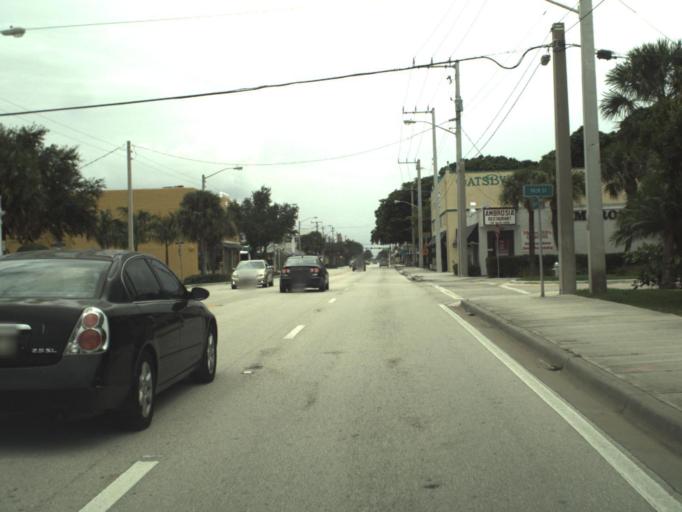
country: US
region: Florida
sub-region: Palm Beach County
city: West Palm Beach
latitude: 26.6997
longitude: -80.0541
